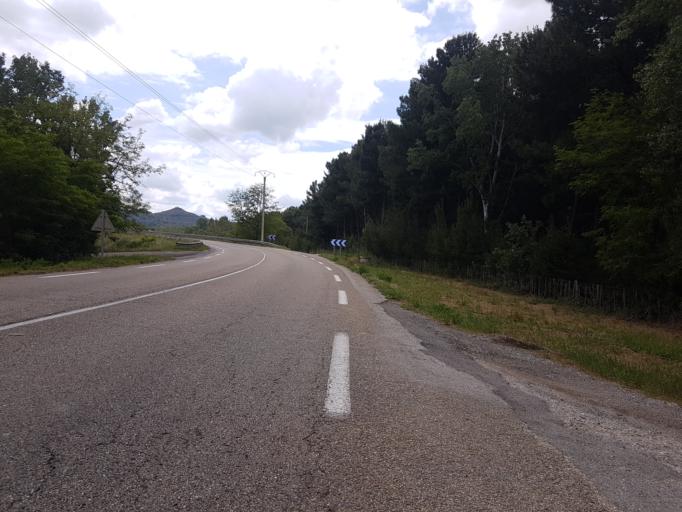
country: FR
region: Languedoc-Roussillon
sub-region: Departement du Gard
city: Vallabregues
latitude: 43.8648
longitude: 4.6191
